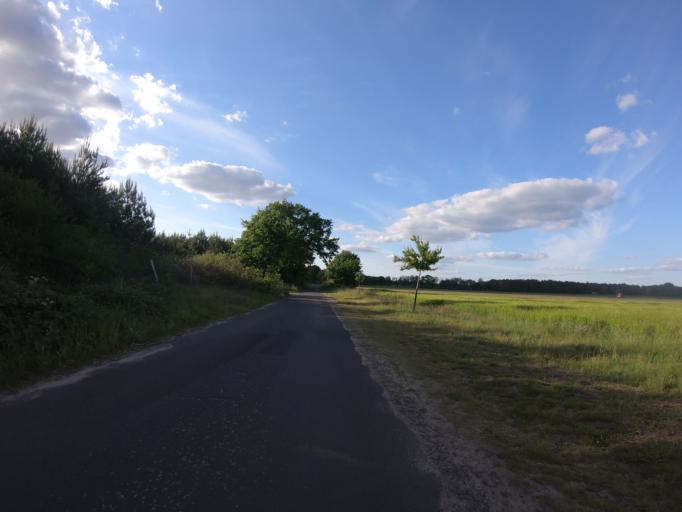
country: DE
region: Lower Saxony
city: Wagenhoff
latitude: 52.5178
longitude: 10.4718
